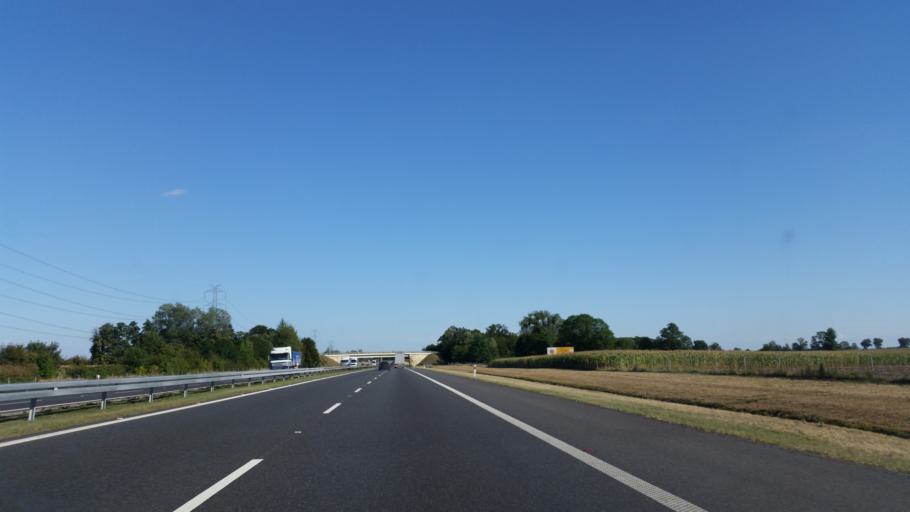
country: PL
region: Lower Silesian Voivodeship
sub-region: Powiat olawski
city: Wierzbno
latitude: 50.9217
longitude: 17.1329
